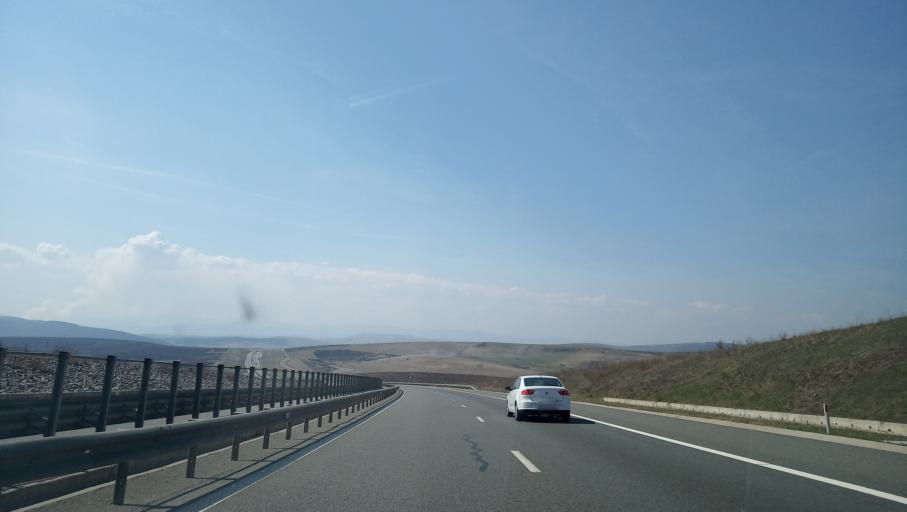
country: RO
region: Cluj
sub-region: Comuna Tureni
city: Tureni
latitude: 46.6038
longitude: 23.6950
